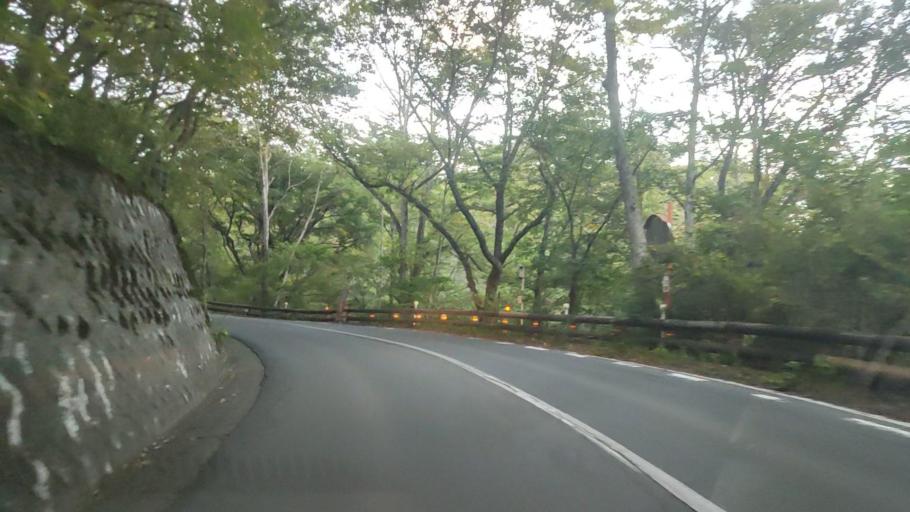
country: JP
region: Nagano
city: Komoro
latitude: 36.3800
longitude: 138.5916
